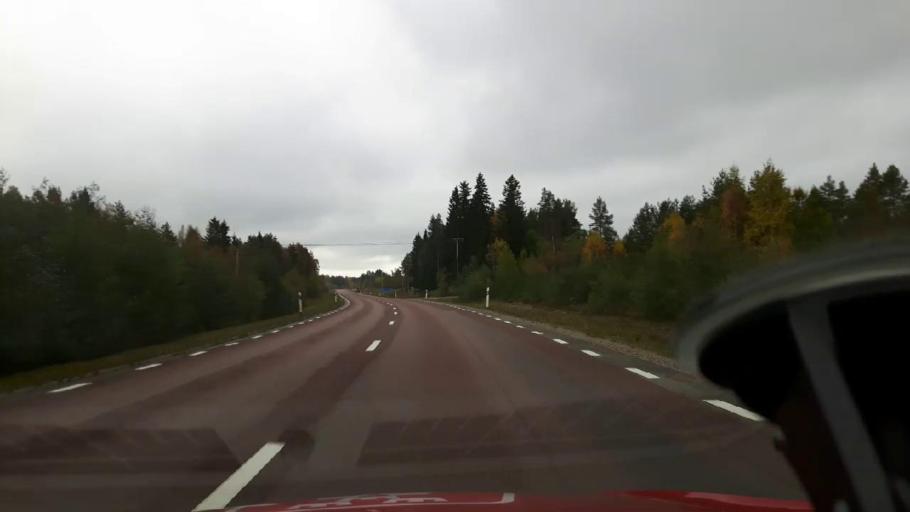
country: SE
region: Jaemtland
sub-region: Harjedalens Kommun
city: Sveg
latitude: 62.2683
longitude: 14.8052
